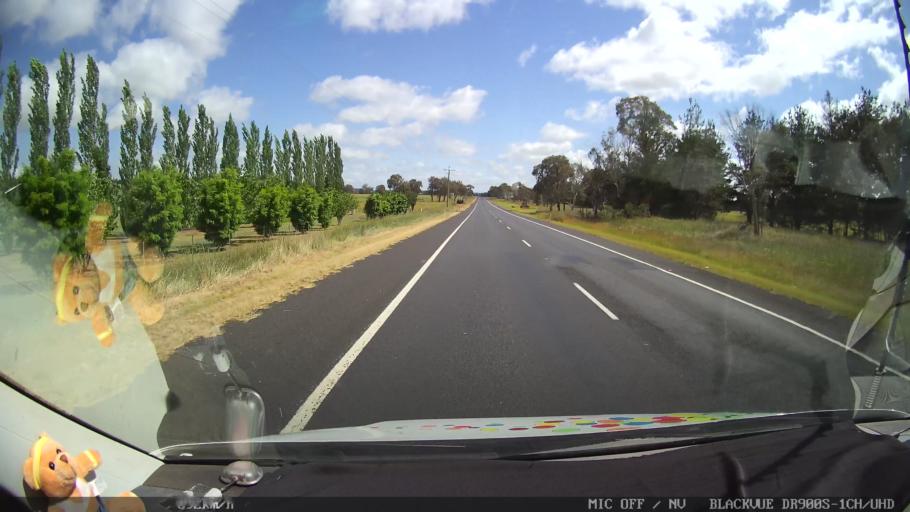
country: AU
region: New South Wales
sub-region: Glen Innes Severn
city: Glen Innes
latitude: -29.8762
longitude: 151.7344
